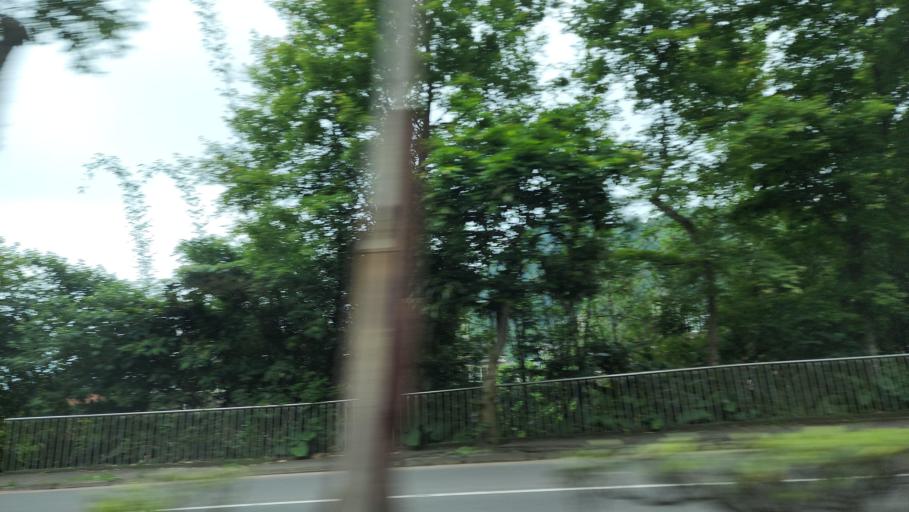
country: TW
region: Taiwan
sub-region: Keelung
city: Keelung
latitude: 25.1611
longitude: 121.6926
